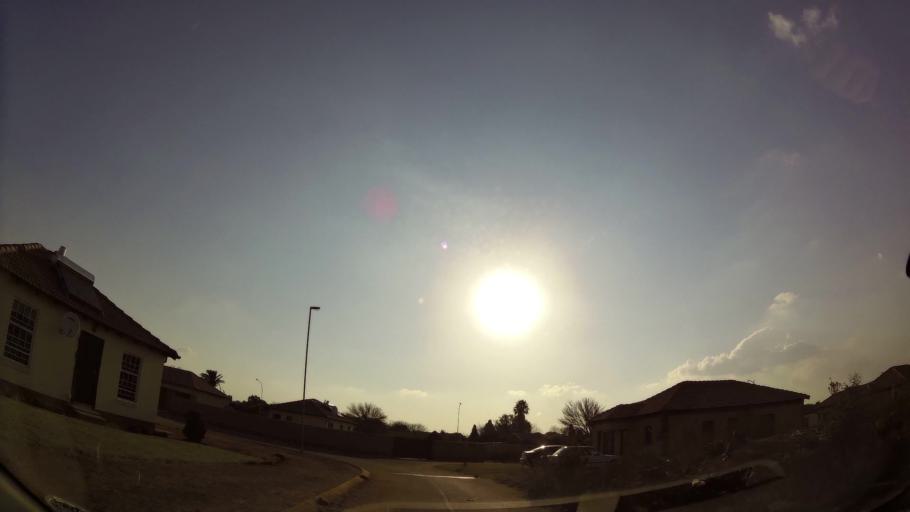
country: ZA
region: Gauteng
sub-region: Ekurhuleni Metropolitan Municipality
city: Benoni
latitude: -26.1403
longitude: 28.3746
